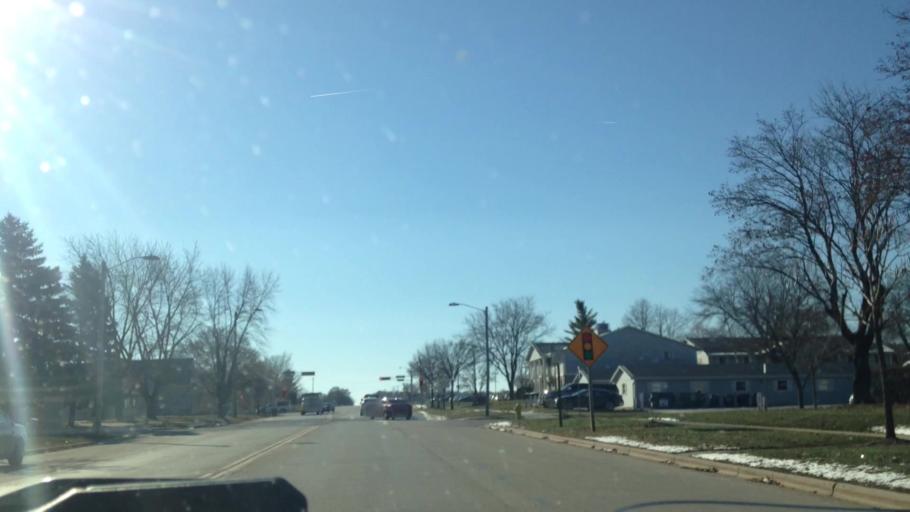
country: US
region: Wisconsin
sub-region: Washington County
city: West Bend
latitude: 43.4138
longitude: -88.1613
